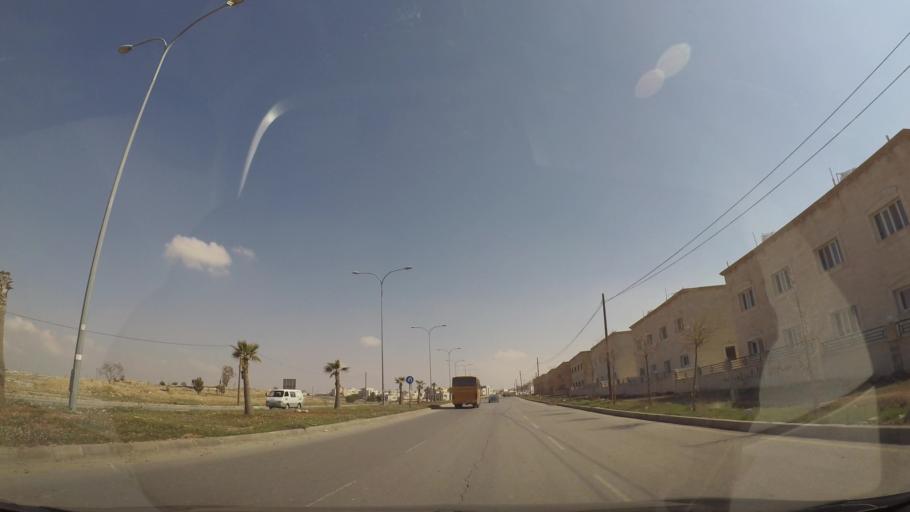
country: JO
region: Zarqa
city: Zarqa
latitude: 32.0644
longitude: 36.1107
